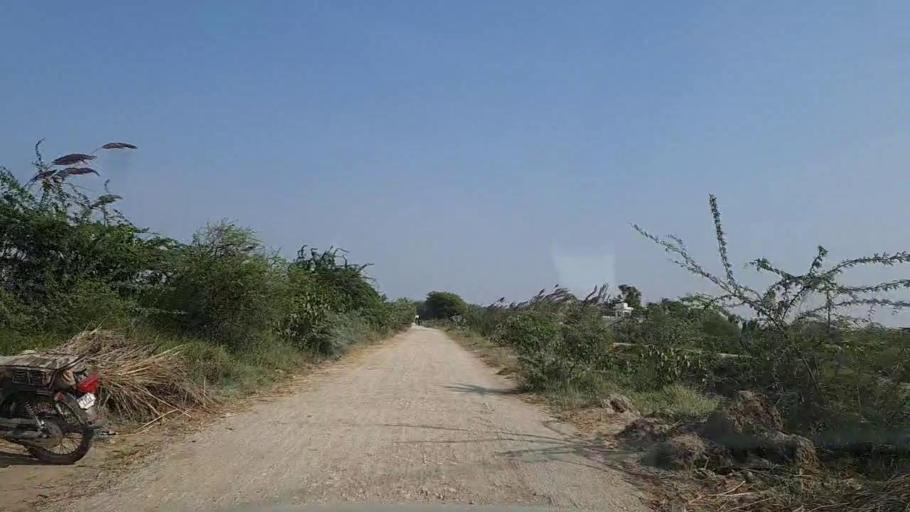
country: PK
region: Sindh
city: Mirpur Sakro
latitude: 24.5583
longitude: 67.5942
